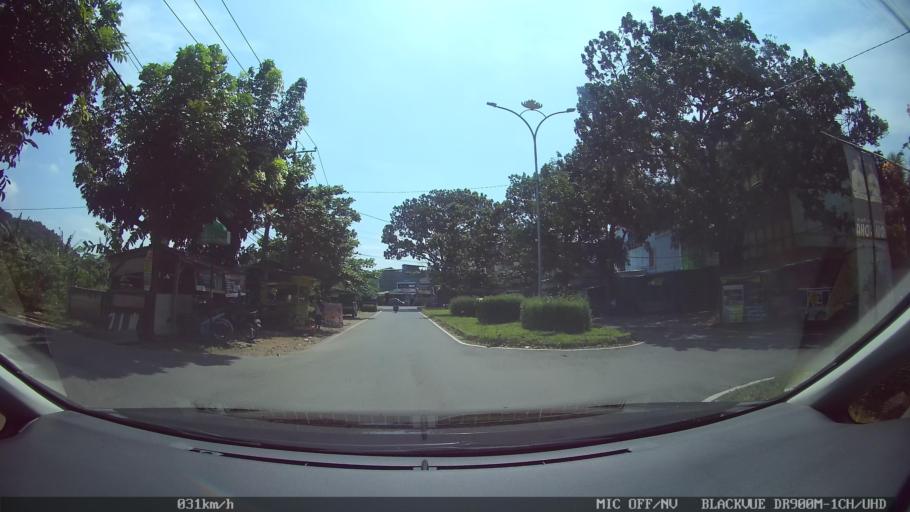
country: ID
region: Lampung
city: Kedaton
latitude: -5.3839
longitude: 105.2724
